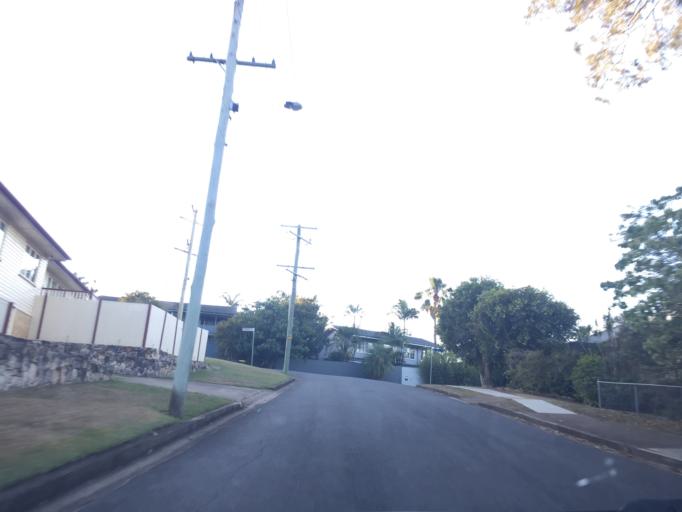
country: AU
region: Queensland
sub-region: Brisbane
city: Taringa
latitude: -27.4546
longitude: 152.9500
